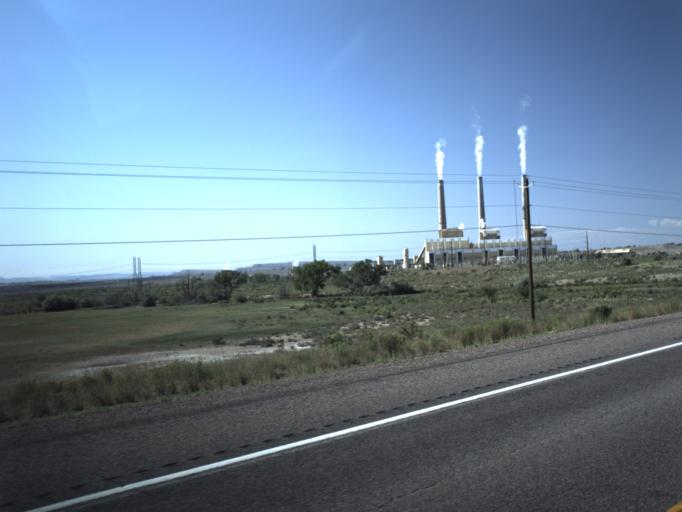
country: US
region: Utah
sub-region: Emery County
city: Castle Dale
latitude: 39.1903
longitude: -111.0255
